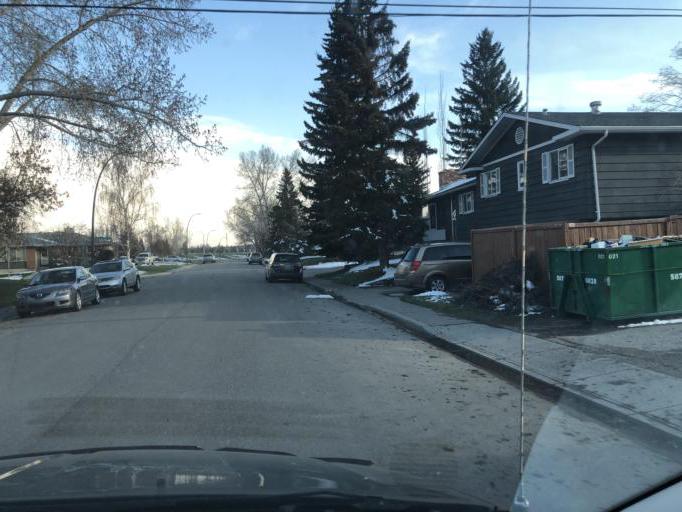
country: CA
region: Alberta
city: Calgary
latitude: 50.9403
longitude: -114.0333
